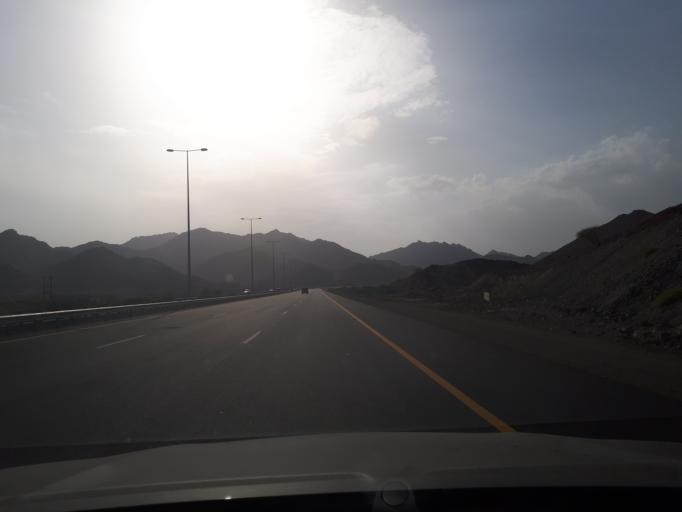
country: OM
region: Ash Sharqiyah
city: Ibra'
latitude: 22.8485
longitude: 58.3258
